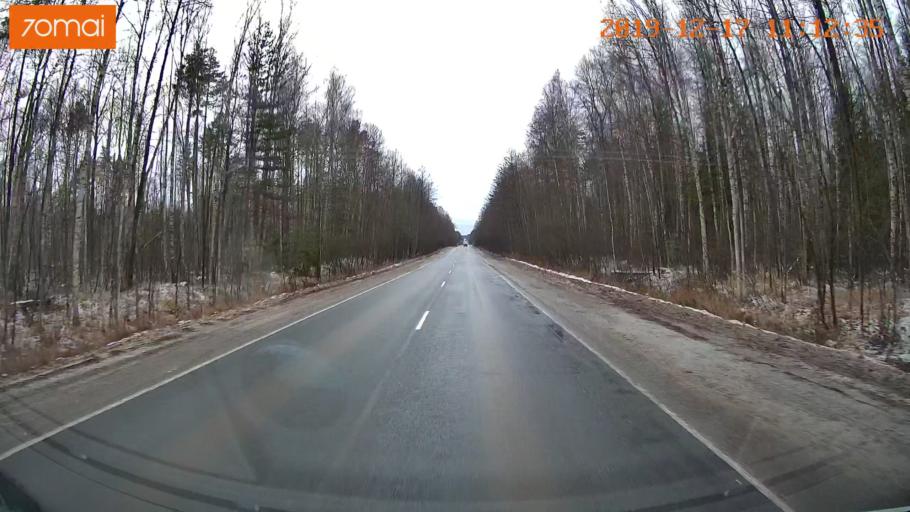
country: RU
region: Vladimir
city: Gus'-Khrustal'nyy
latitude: 55.5739
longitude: 40.6269
